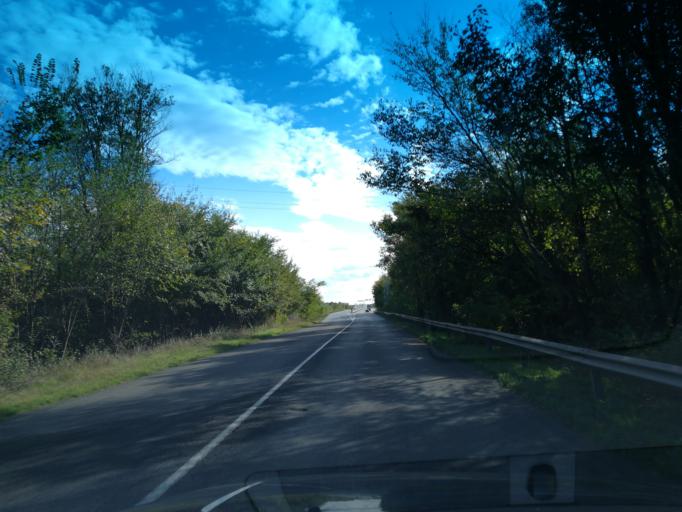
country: BG
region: Stara Zagora
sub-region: Obshtina Stara Zagora
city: Stara Zagora
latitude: 42.3470
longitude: 25.6597
